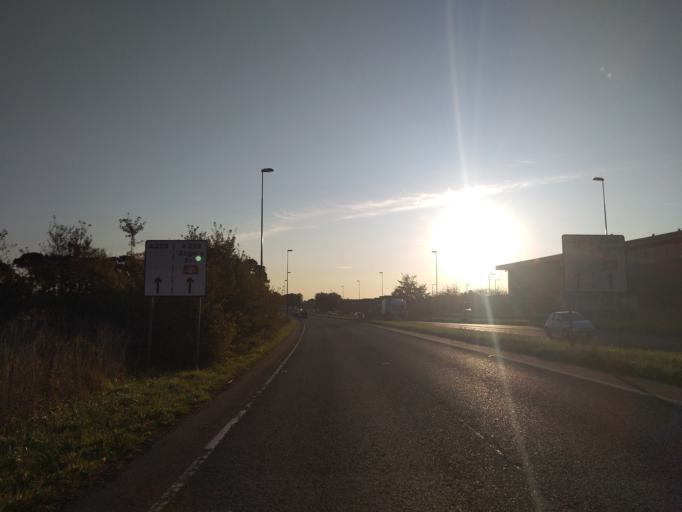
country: GB
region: England
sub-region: West Sussex
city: Rustington
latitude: 50.8185
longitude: -0.4958
